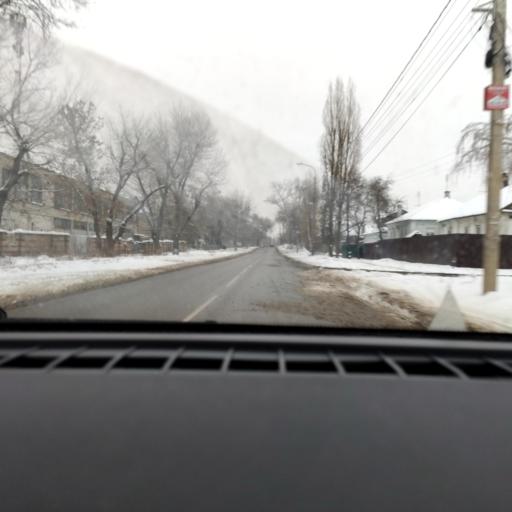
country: RU
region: Voronezj
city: Maslovka
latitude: 51.6107
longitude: 39.2282
